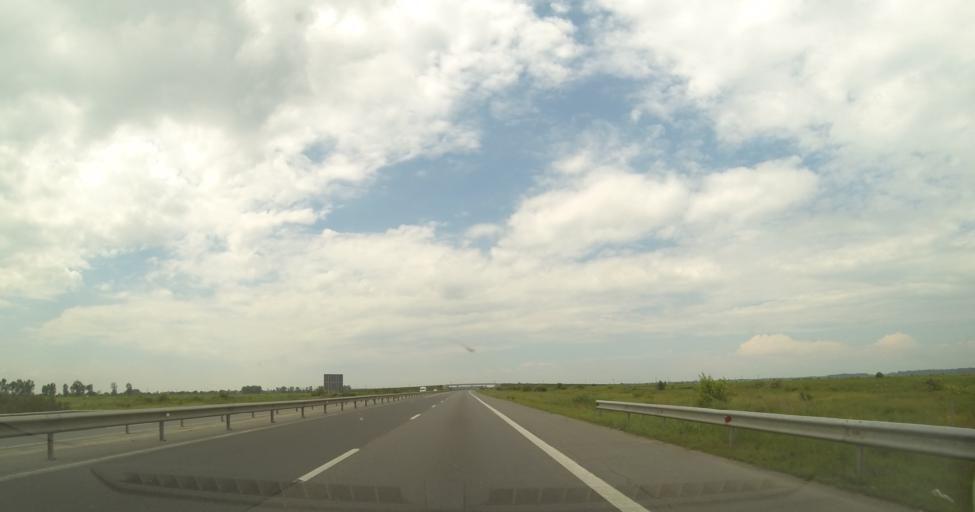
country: RO
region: Dambovita
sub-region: Comuna Corbii Mari
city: Corbii Mari
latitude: 44.5424
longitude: 25.5163
